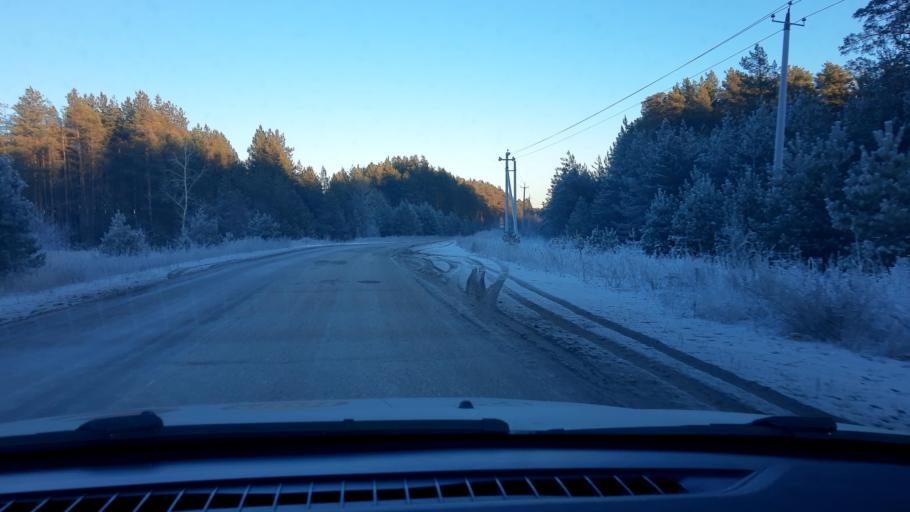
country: RU
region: Nizjnij Novgorod
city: Mulino
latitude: 56.3162
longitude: 42.9729
